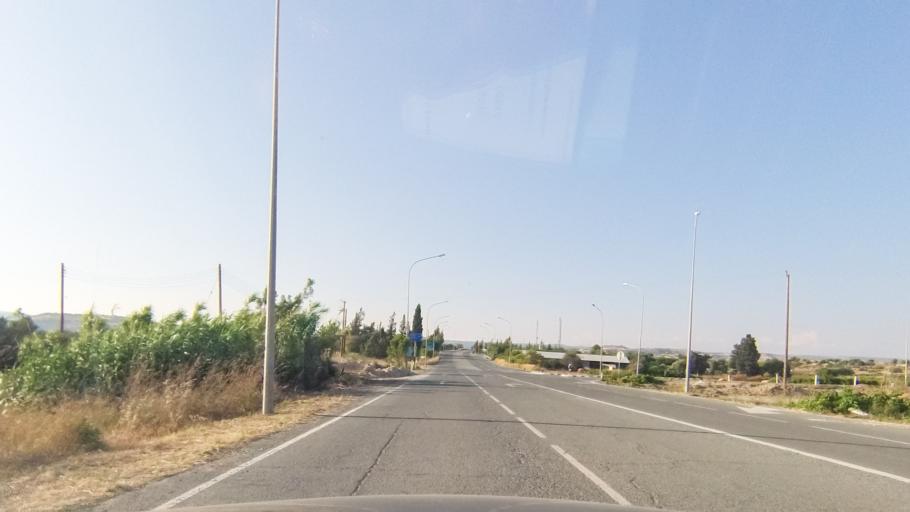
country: CY
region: Limassol
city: Pissouri
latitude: 34.6789
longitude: 32.7601
